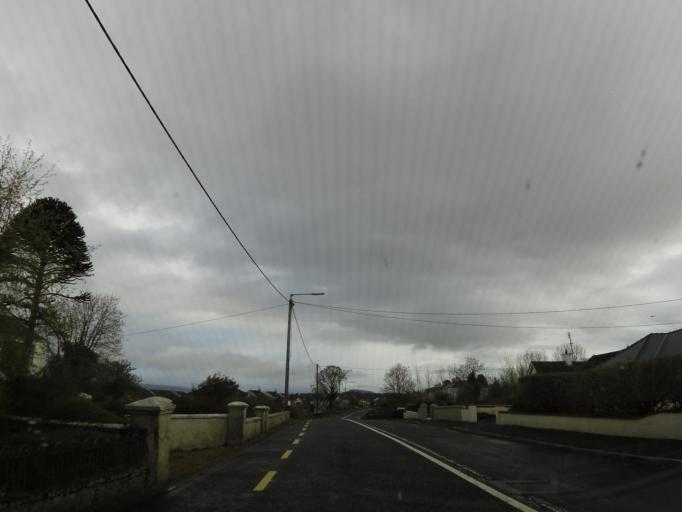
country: IE
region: Connaught
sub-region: Sligo
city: Tobercurry
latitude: 54.0472
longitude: -8.7375
